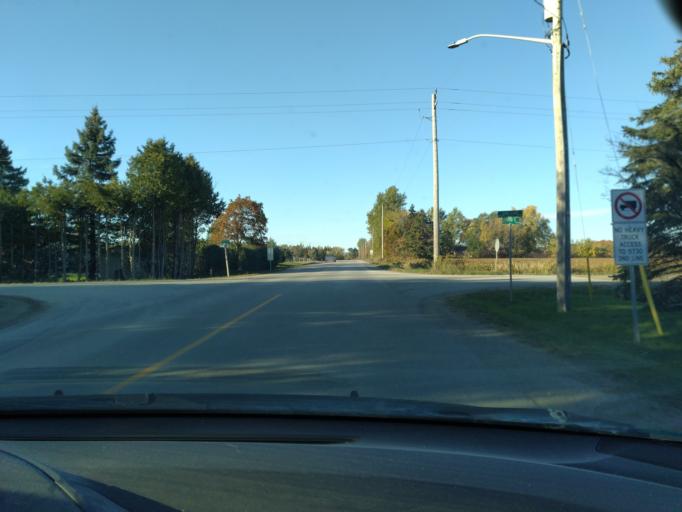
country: CA
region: Ontario
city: Bradford West Gwillimbury
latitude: 44.0137
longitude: -79.7249
